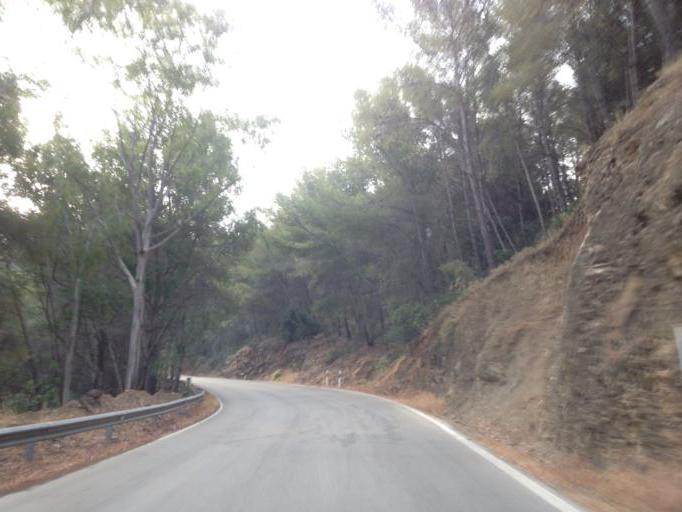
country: ES
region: Andalusia
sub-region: Provincia de Malaga
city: Malaga
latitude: 36.7669
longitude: -4.4013
